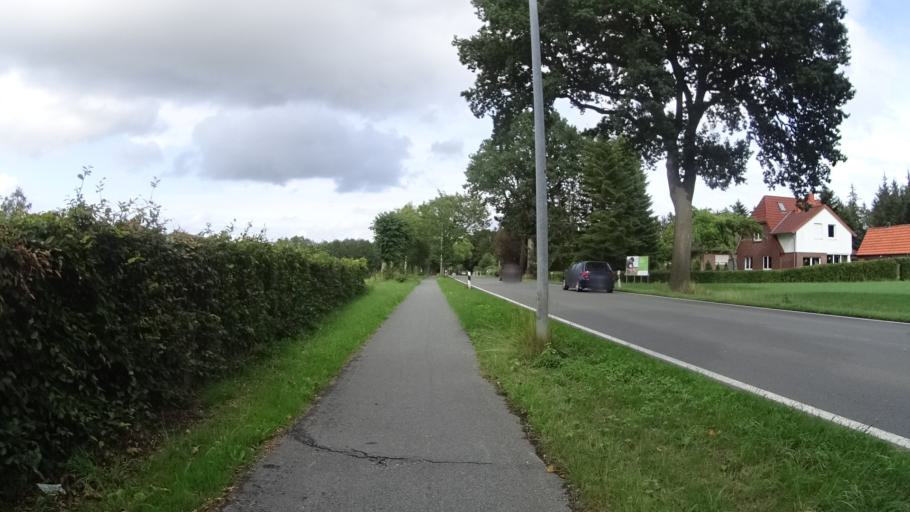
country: DE
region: Lower Saxony
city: Varel
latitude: 53.3904
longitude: 8.0850
